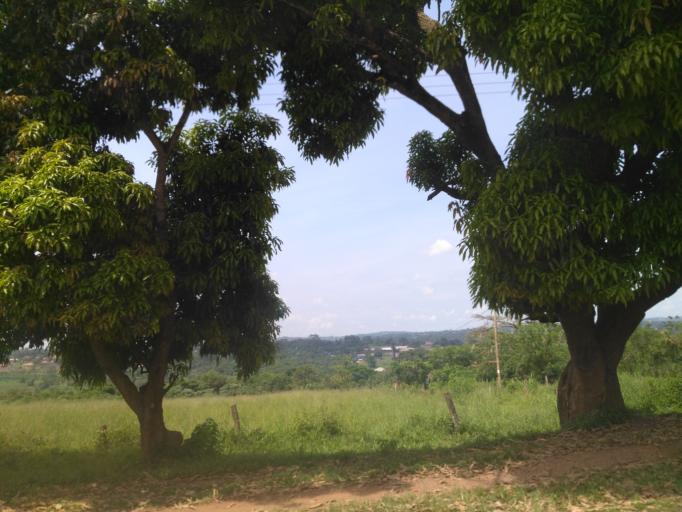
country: UG
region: Central Region
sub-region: Wakiso District
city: Bweyogerere
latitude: 0.4683
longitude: 32.6058
